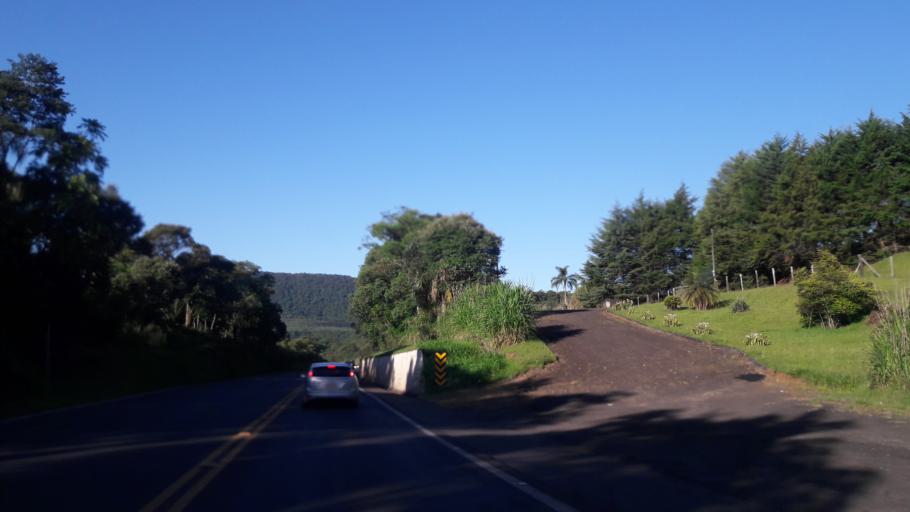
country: BR
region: Parana
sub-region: Prudentopolis
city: Prudentopolis
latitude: -25.3231
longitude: -51.1911
